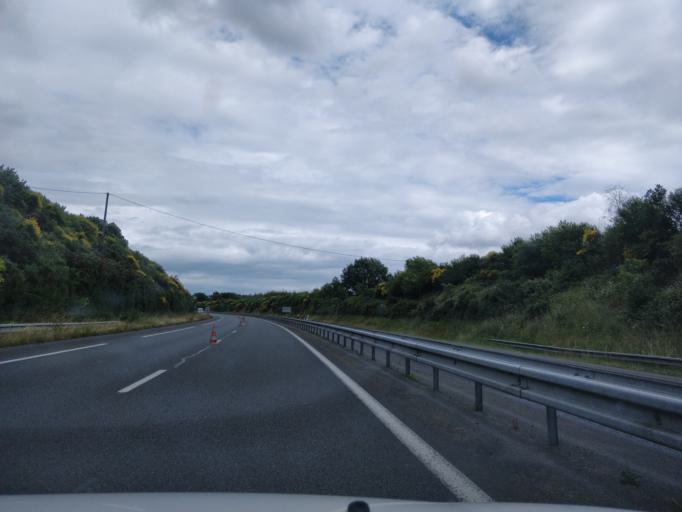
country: FR
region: Pays de la Loire
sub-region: Departement de Maine-et-Loire
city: Noyant-la-Gravoyere
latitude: 47.7064
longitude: -0.9832
